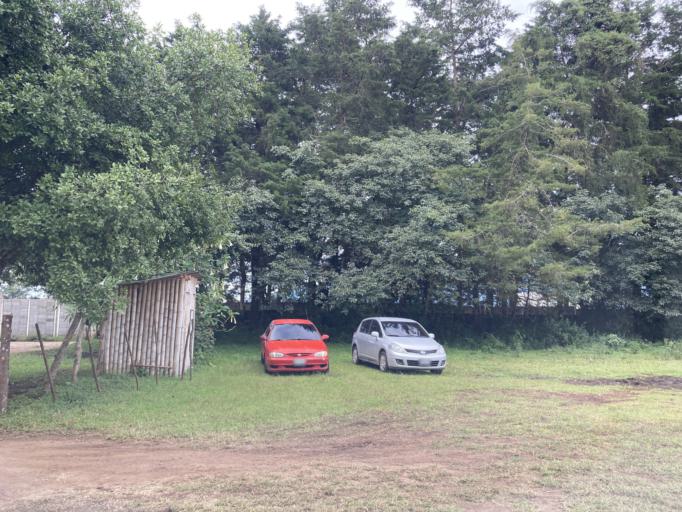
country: GT
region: Guatemala
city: San Jose Pinula
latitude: 14.5313
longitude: -90.4038
